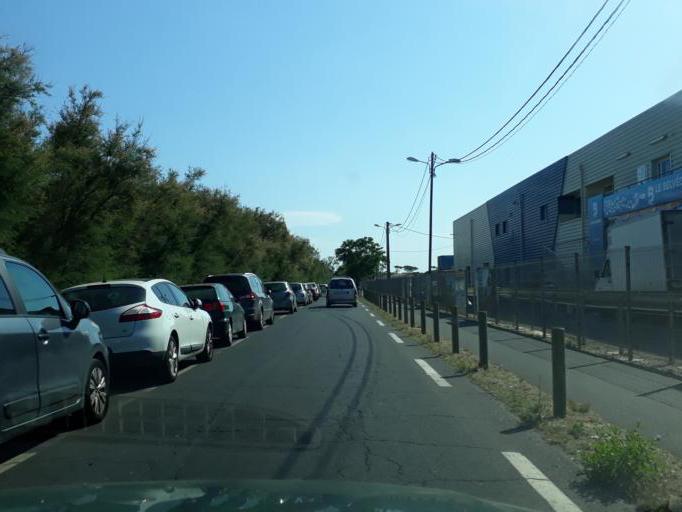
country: FR
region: Languedoc-Roussillon
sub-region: Departement de l'Herault
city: Agde
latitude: 43.2925
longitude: 3.4480
